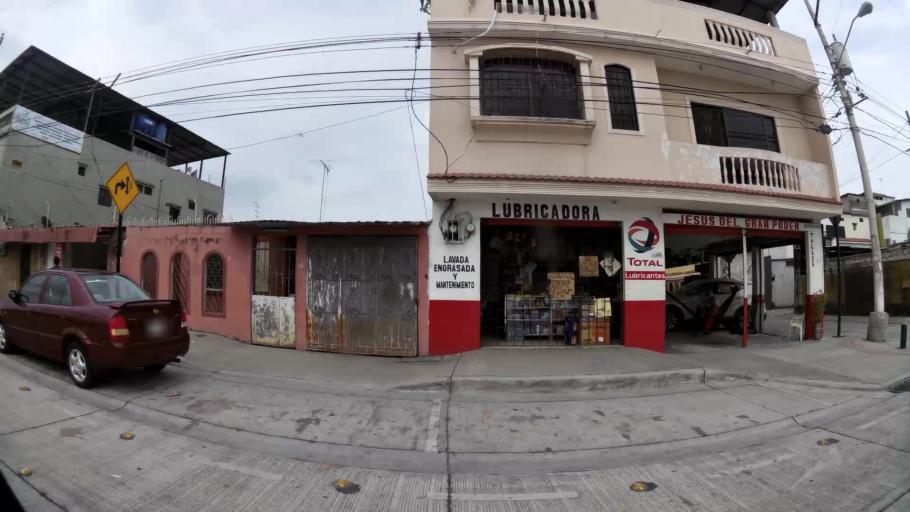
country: EC
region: Guayas
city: Eloy Alfaro
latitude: -2.1198
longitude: -79.9000
